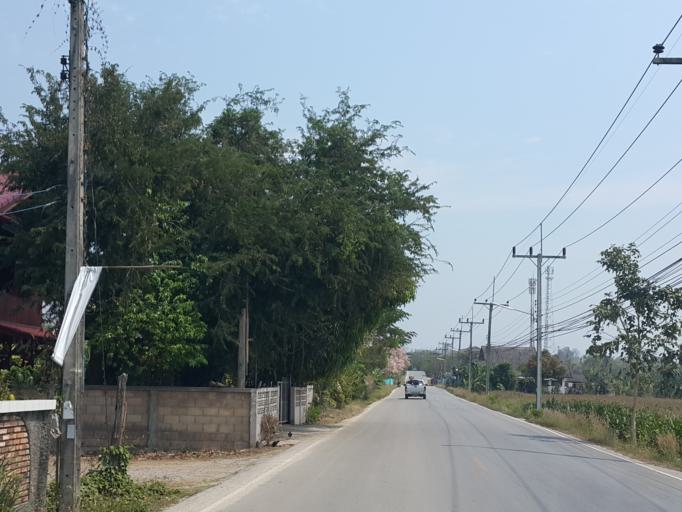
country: TH
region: Lampang
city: Chae Hom
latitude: 18.7581
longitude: 99.5647
